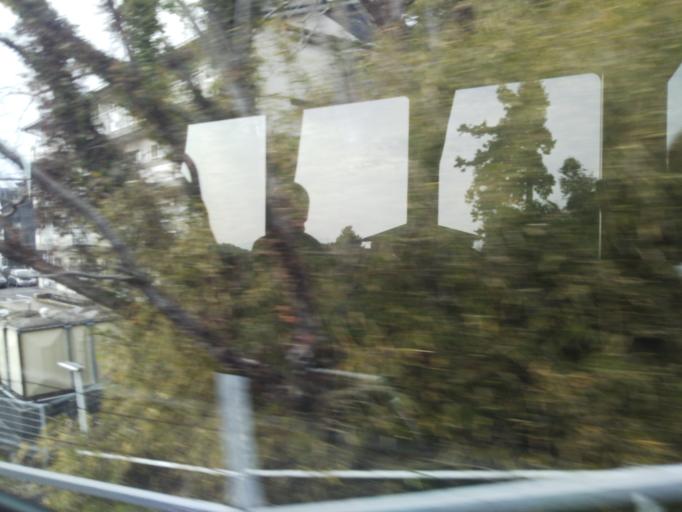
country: JP
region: Kochi
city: Nakamura
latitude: 32.9817
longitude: 132.9557
